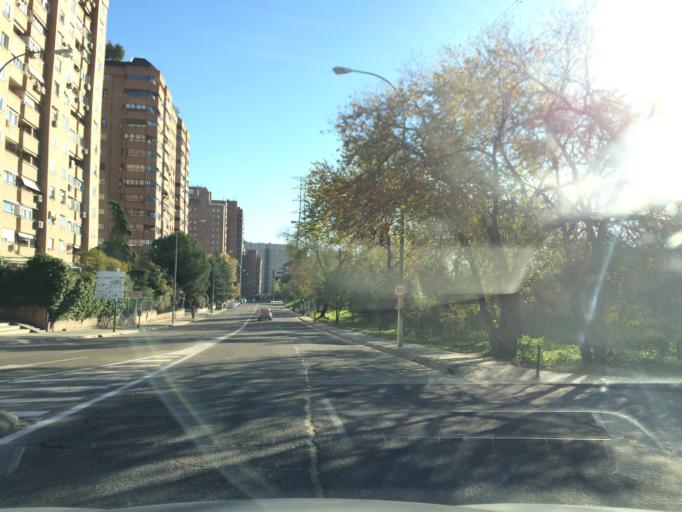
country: ES
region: Madrid
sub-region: Provincia de Madrid
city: Pinar de Chamartin
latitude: 40.4805
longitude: -3.6758
